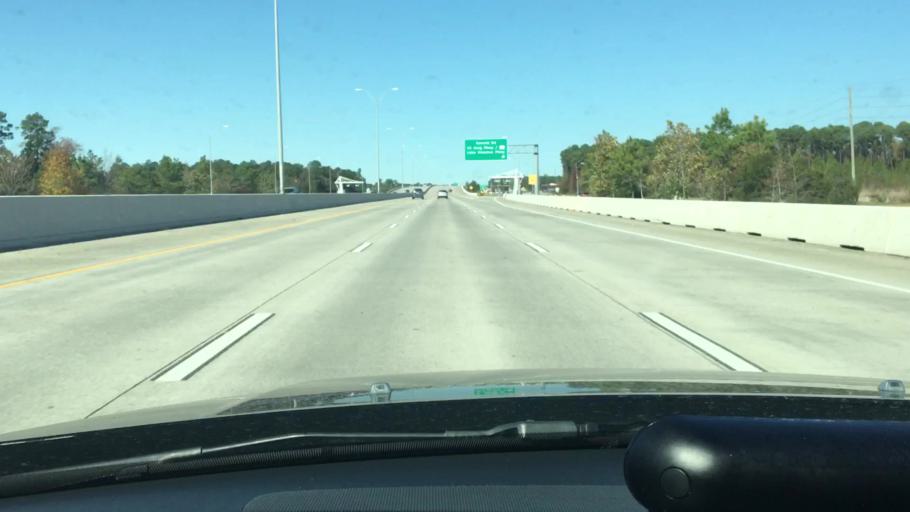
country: US
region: Texas
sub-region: Harris County
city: Sheldon
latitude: 29.8775
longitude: -95.1928
